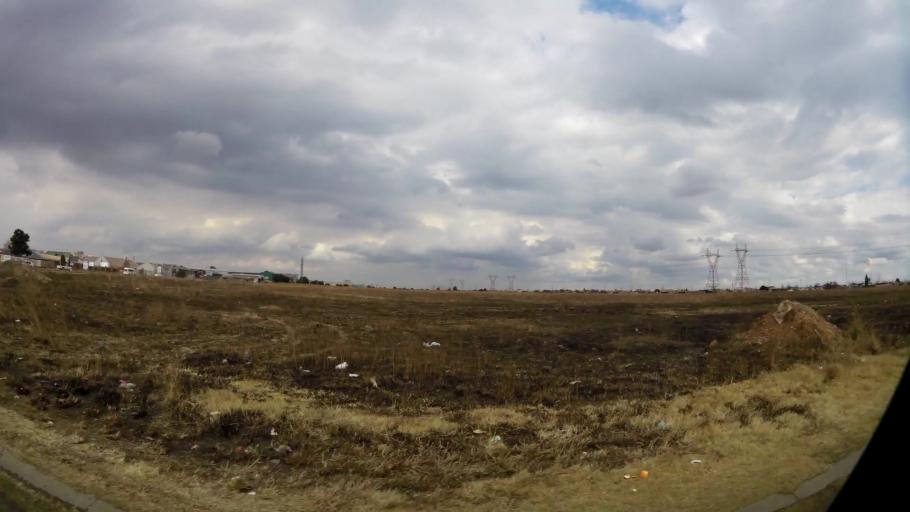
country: ZA
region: Gauteng
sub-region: Sedibeng District Municipality
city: Vanderbijlpark
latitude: -26.6776
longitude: 27.7929
